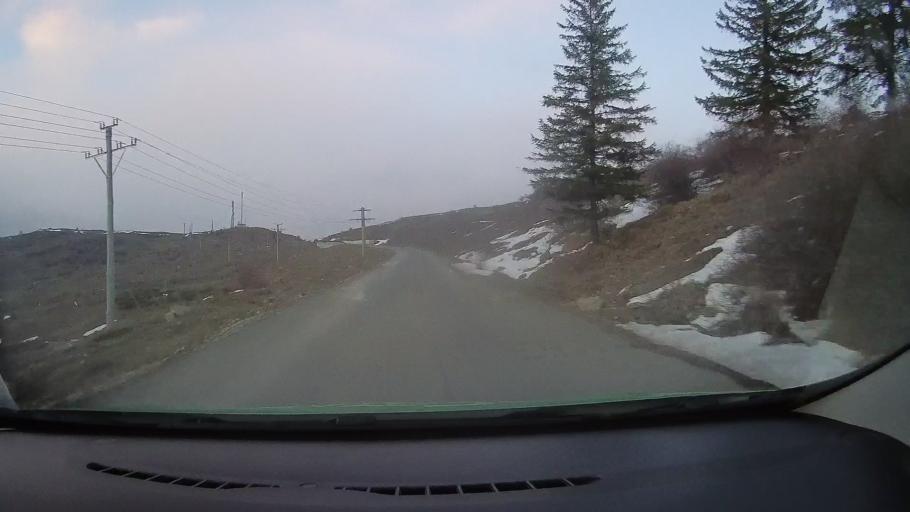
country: RO
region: Prahova
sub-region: Comuna Secaria
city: Secaria
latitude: 45.2807
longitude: 25.7005
